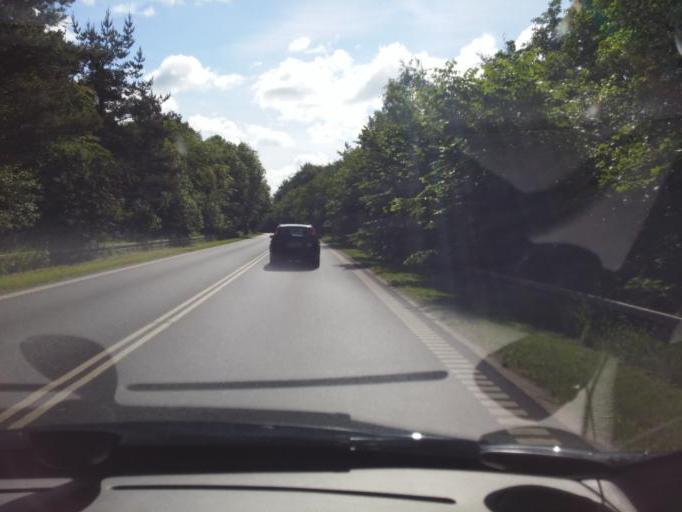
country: DK
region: Capital Region
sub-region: Hillerod Kommune
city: Hillerod
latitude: 55.9533
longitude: 12.2995
